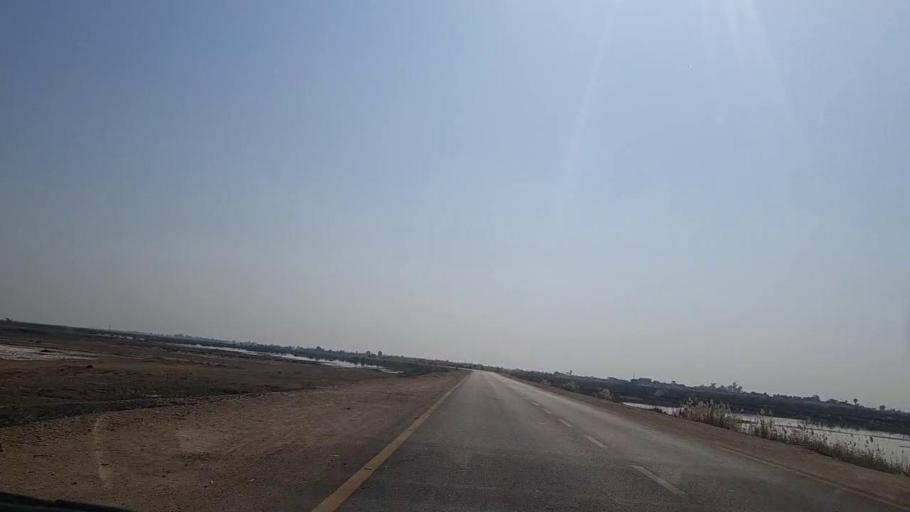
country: PK
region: Sindh
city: Sakrand
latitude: 26.0836
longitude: 68.4026
